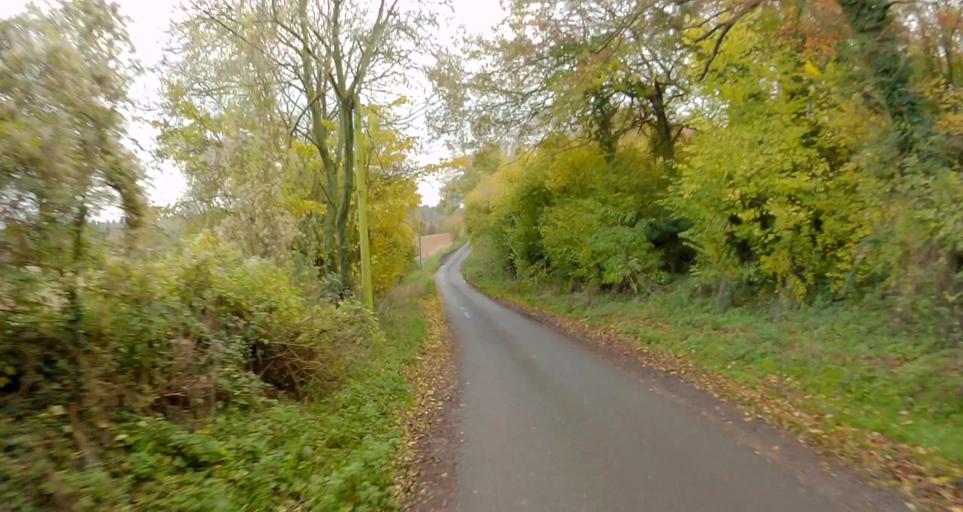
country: GB
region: England
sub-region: Hampshire
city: Long Sutton
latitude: 51.2139
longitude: -0.9614
